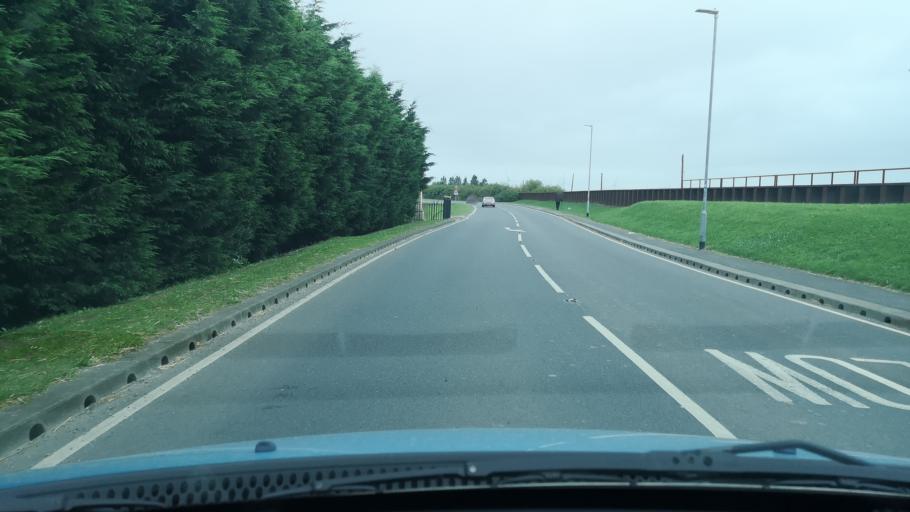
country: GB
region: England
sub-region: East Riding of Yorkshire
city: Skelton
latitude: 53.6885
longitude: -0.8405
